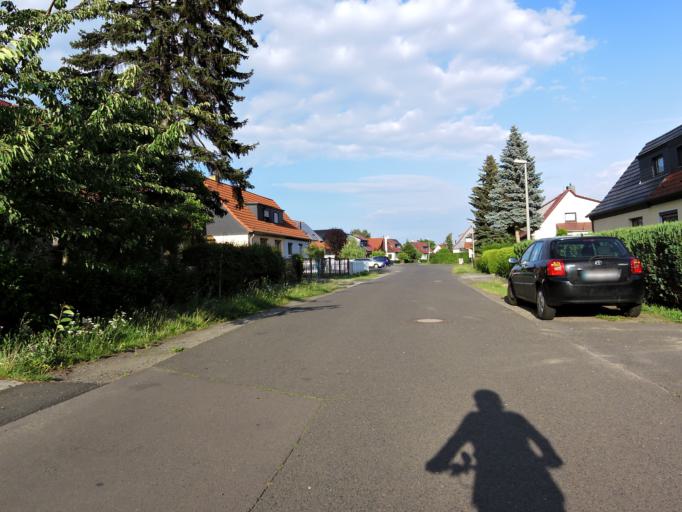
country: DE
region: Saxony
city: Zwenkau
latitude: 51.2721
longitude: 12.2984
